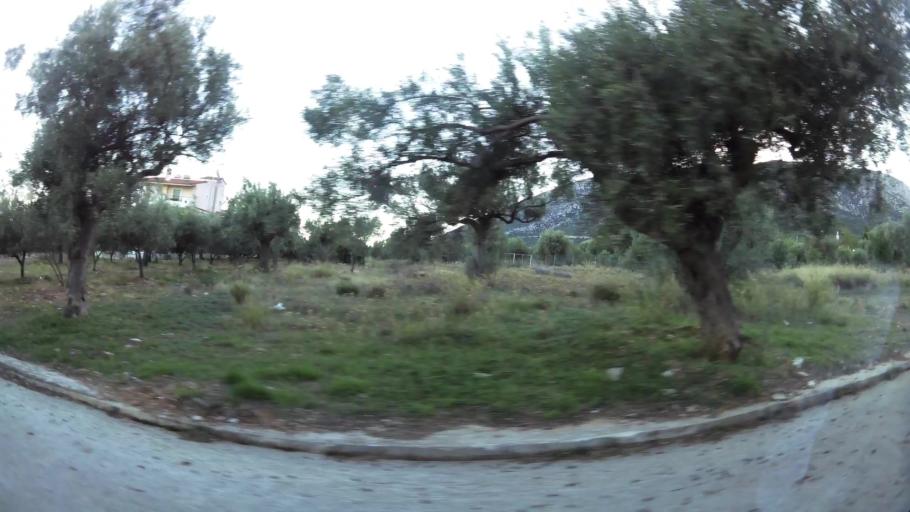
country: GR
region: Attica
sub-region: Nomarchia Anatolikis Attikis
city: Paiania
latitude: 37.9708
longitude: 23.8416
